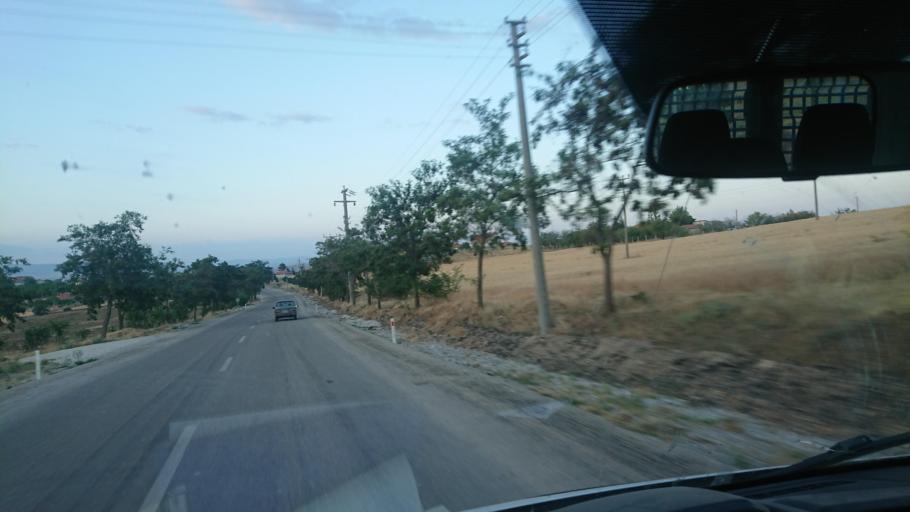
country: TR
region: Aksaray
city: Sariyahsi
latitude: 38.9750
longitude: 33.8341
